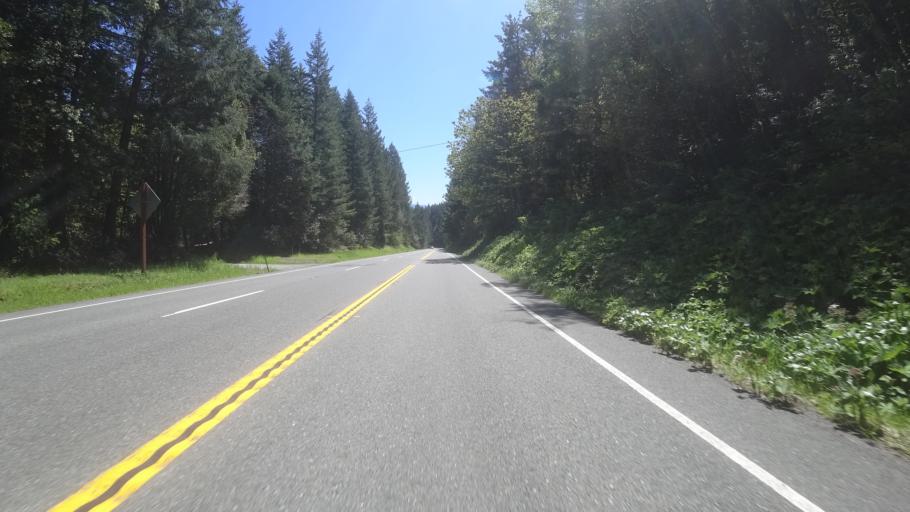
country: US
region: California
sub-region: Humboldt County
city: Blue Lake
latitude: 40.9205
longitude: -123.8358
